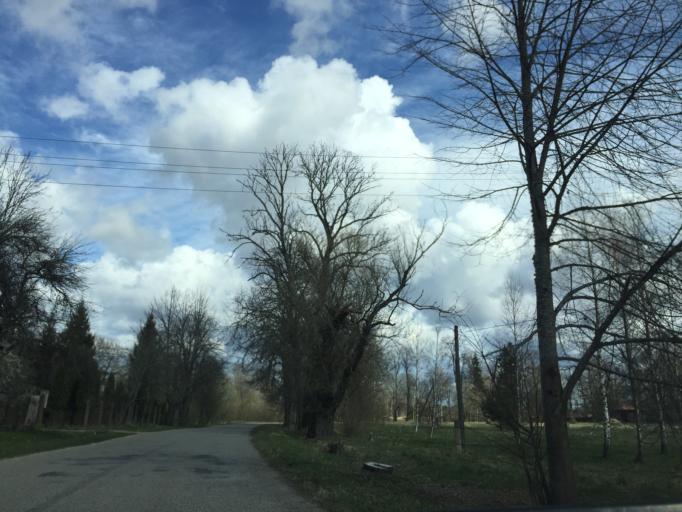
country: LV
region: Limbazu Rajons
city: Limbazi
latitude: 57.6121
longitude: 24.6608
